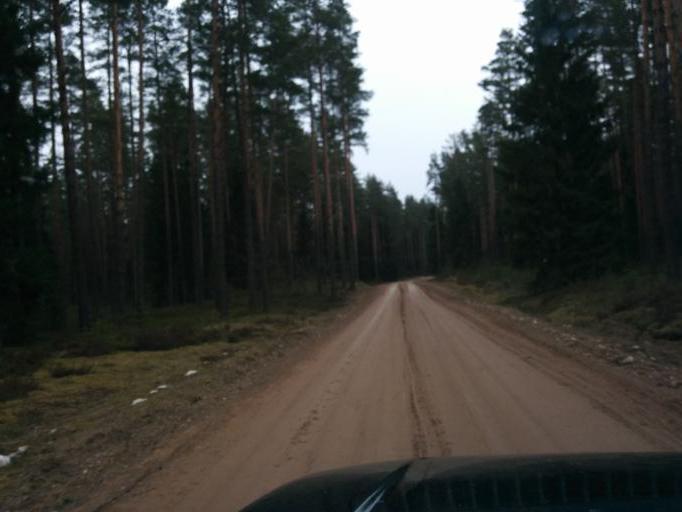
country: LV
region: Ogre
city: Ogre
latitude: 56.7808
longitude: 24.6064
